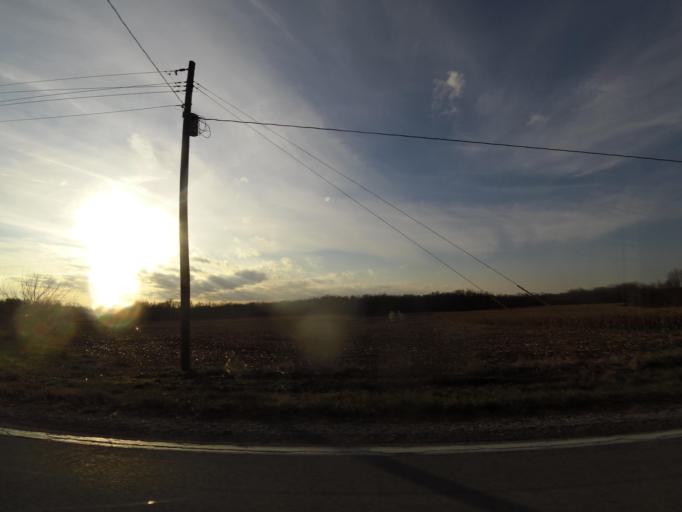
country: US
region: Illinois
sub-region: Fayette County
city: Vandalia
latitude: 38.9240
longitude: -89.2443
